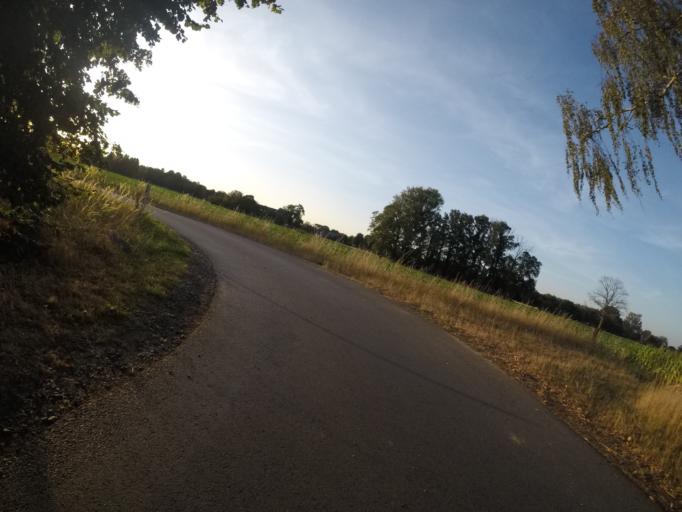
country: DE
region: North Rhine-Westphalia
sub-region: Regierungsbezirk Munster
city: Isselburg
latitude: 51.8601
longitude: 6.5216
